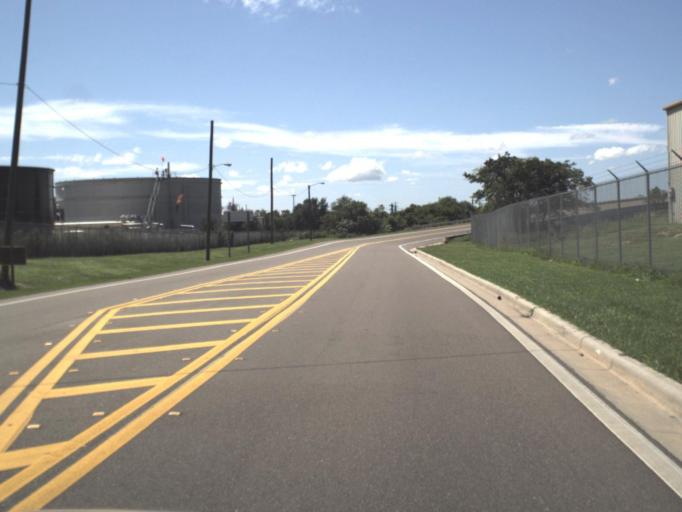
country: US
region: Florida
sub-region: Polk County
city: Auburndale
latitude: 28.0531
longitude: -81.7886
